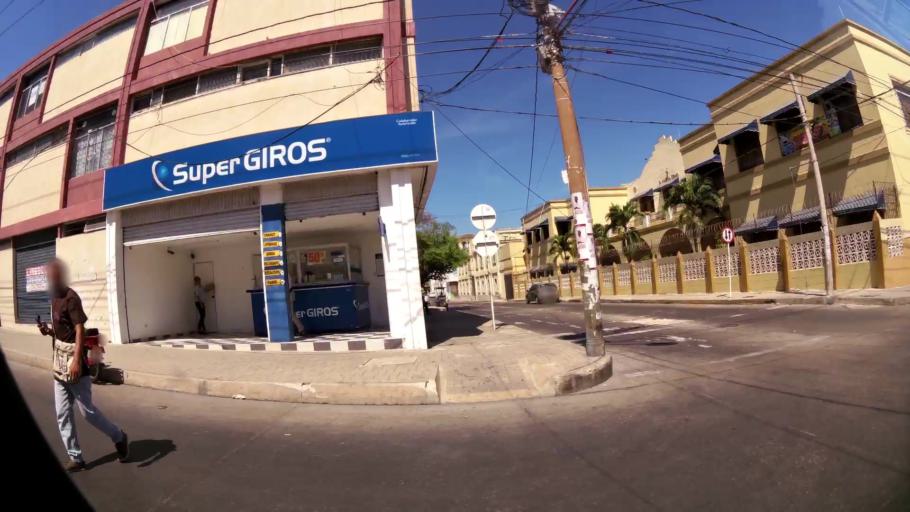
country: CO
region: Atlantico
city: Barranquilla
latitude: 10.9858
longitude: -74.7827
